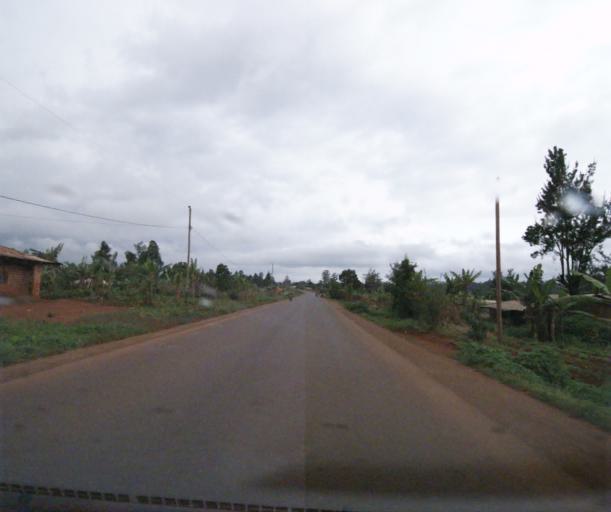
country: CM
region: West
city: Dschang
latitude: 5.4936
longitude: 10.1629
